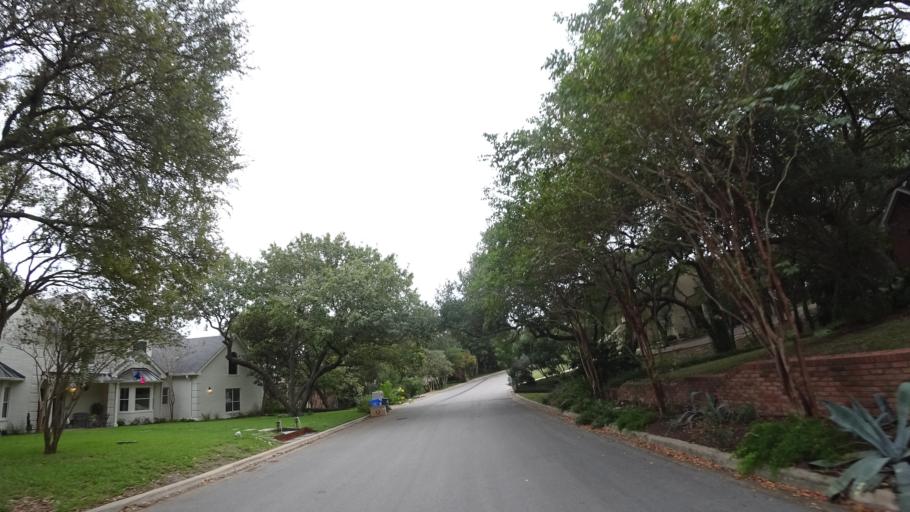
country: US
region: Texas
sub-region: Travis County
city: Rollingwood
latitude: 30.2803
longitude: -97.7861
